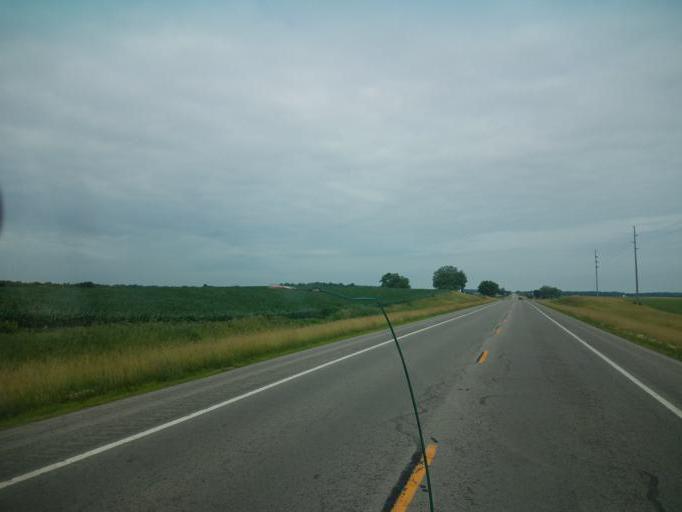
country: US
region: Ohio
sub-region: Hardin County
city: Kenton
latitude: 40.6654
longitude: -83.6527
